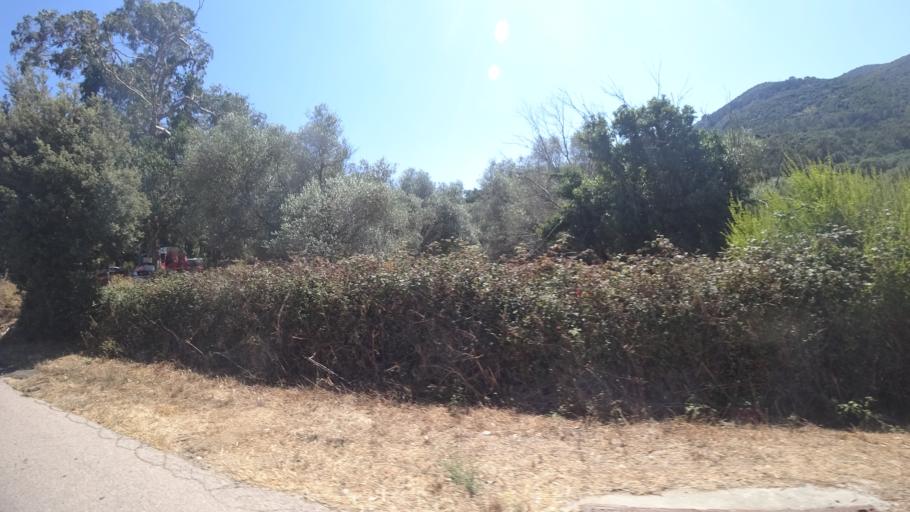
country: FR
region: Corsica
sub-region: Departement de la Corse-du-Sud
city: Alata
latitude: 41.9626
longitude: 8.7248
